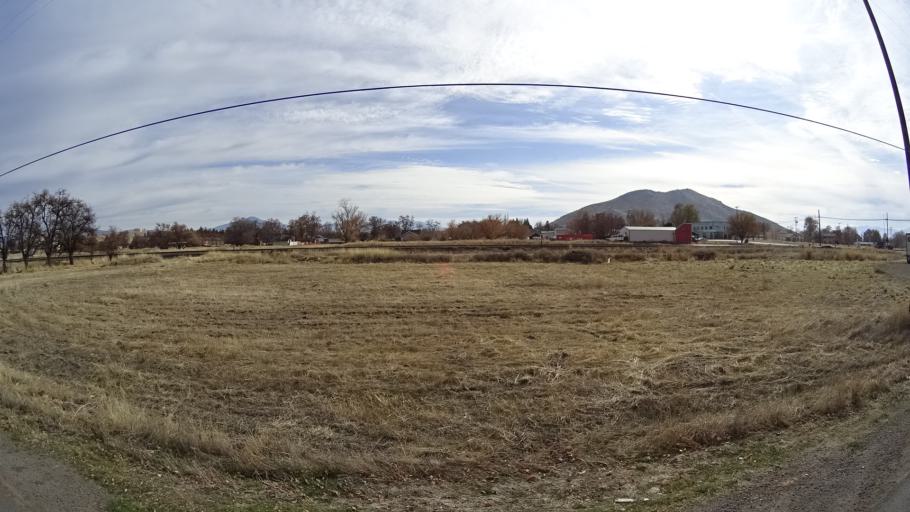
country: US
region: California
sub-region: Siskiyou County
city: Montague
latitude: 41.7290
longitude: -122.5269
